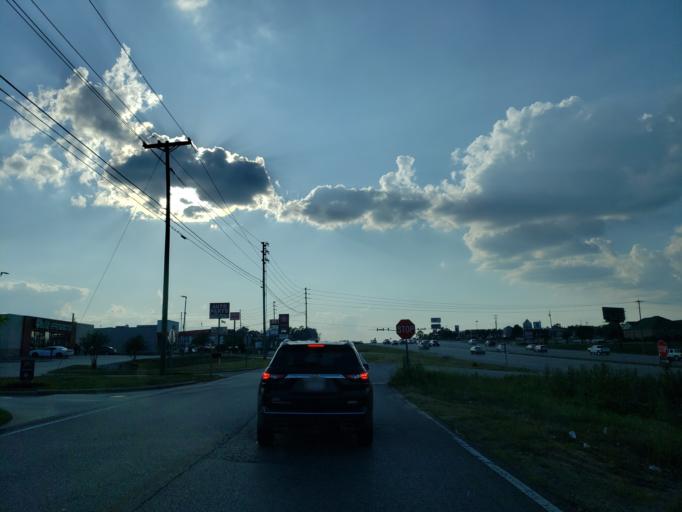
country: US
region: Mississippi
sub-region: Lamar County
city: West Hattiesburg
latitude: 31.3171
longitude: -89.4101
